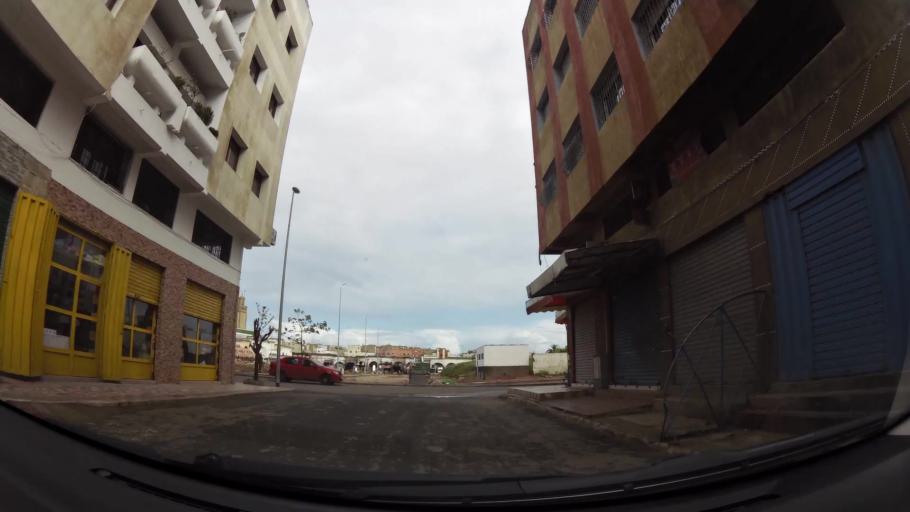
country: MA
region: Grand Casablanca
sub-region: Casablanca
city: Casablanca
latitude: 33.5666
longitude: -7.6730
